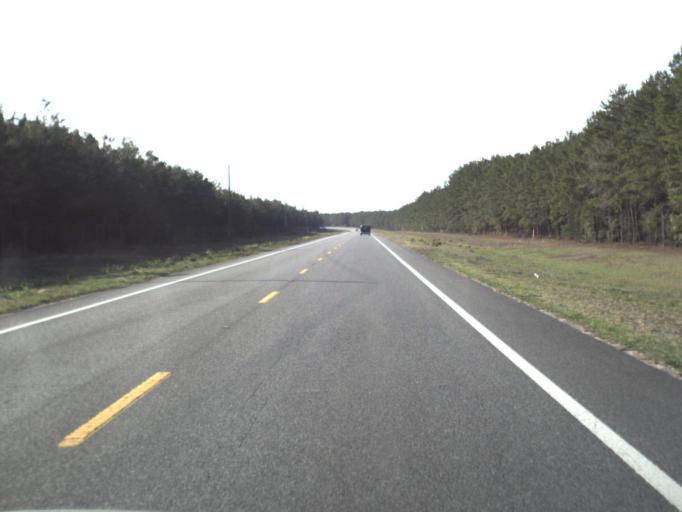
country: US
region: Florida
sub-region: Bay County
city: Lynn Haven
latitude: 30.4351
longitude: -85.6956
